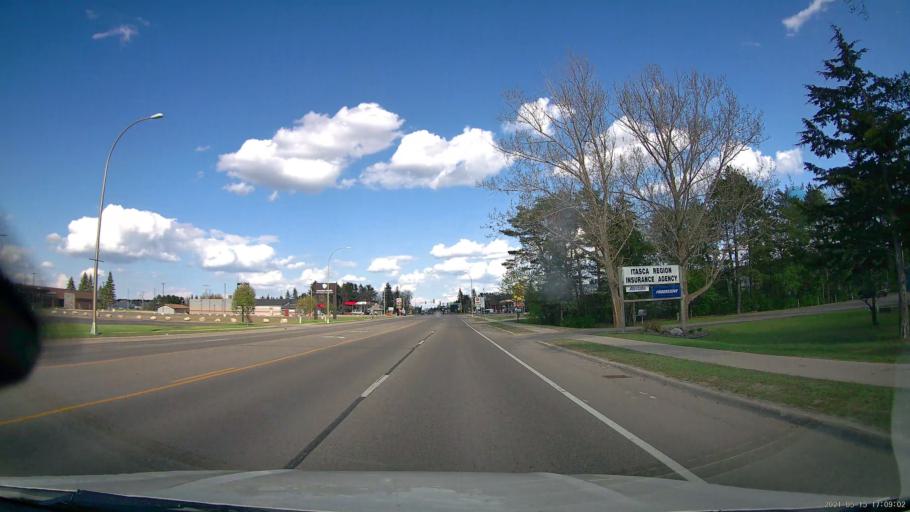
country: US
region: Minnesota
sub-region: Hubbard County
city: Park Rapids
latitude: 46.9218
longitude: -95.0403
